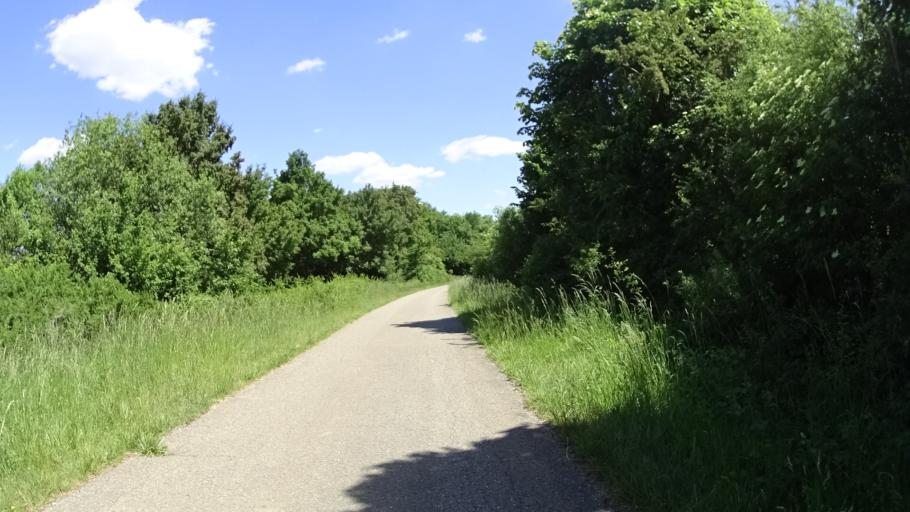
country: DE
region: Bavaria
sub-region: Regierungsbezirk Mittelfranken
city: Thalmassing
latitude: 49.0757
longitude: 11.2799
